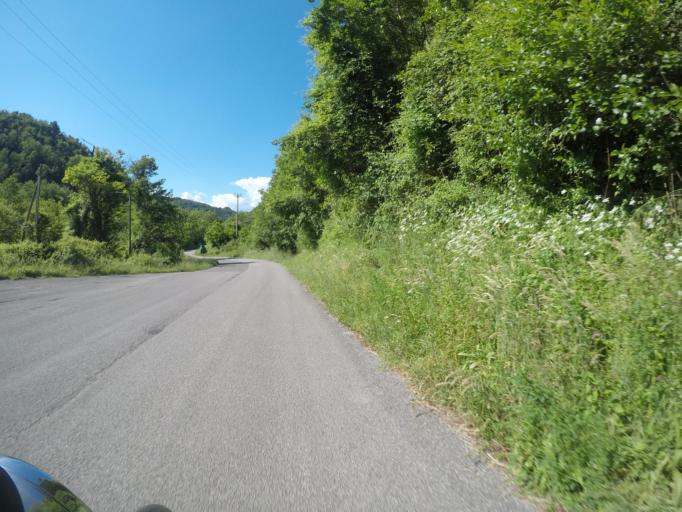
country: IT
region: Tuscany
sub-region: Provincia di Massa-Carrara
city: Fosdinovo
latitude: 44.1470
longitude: 10.0840
